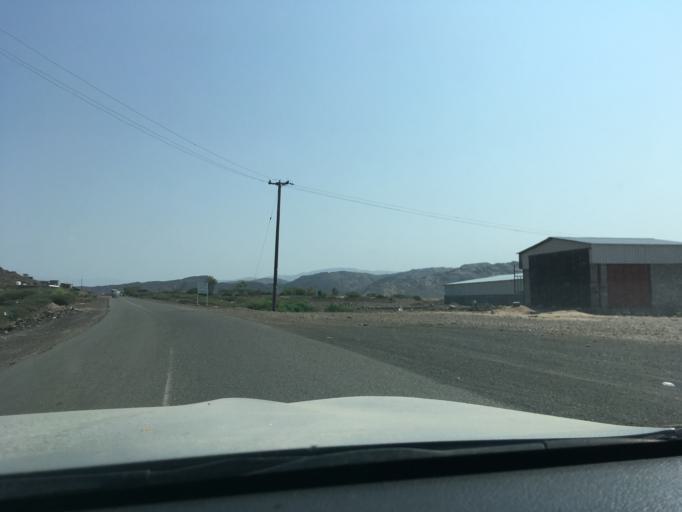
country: YE
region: Lahij
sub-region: Al Milah
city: Al Milah
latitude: 13.4202
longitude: 44.8208
